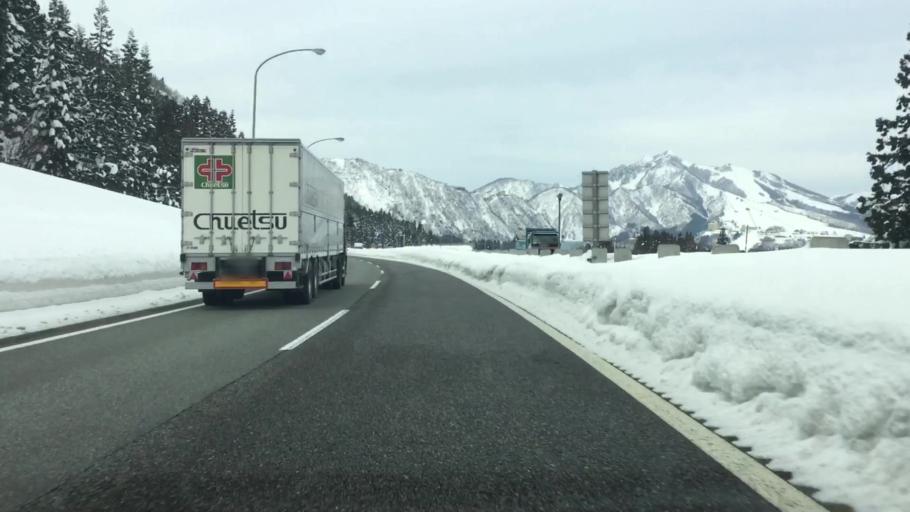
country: JP
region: Niigata
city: Shiozawa
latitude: 36.8906
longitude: 138.8477
